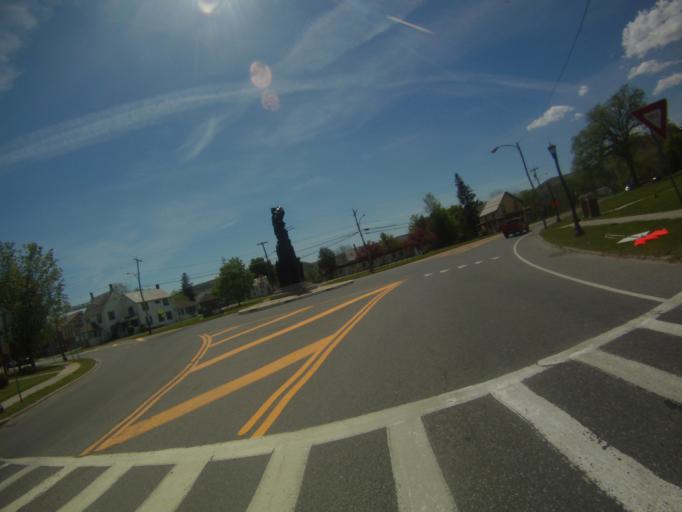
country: US
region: New York
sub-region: Essex County
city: Ticonderoga
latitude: 43.8486
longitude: -73.4350
